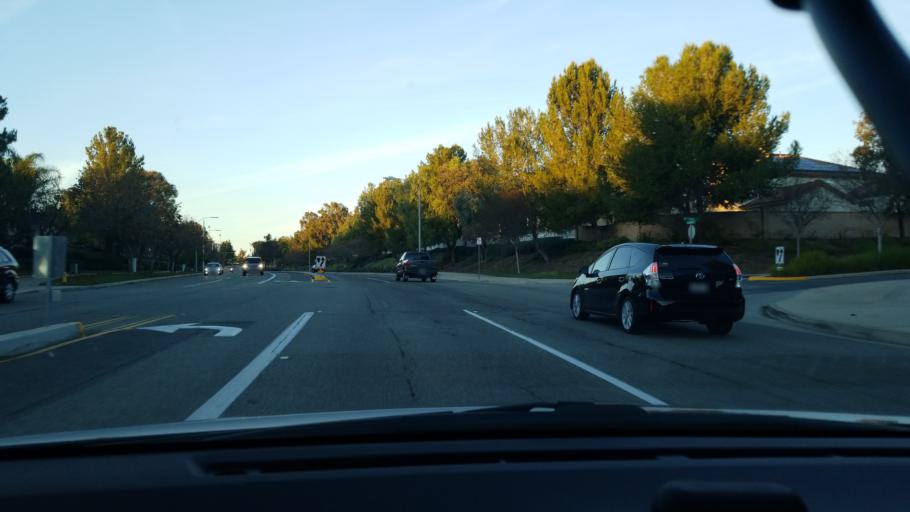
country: US
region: California
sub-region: Riverside County
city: Temecula
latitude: 33.4967
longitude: -117.0950
